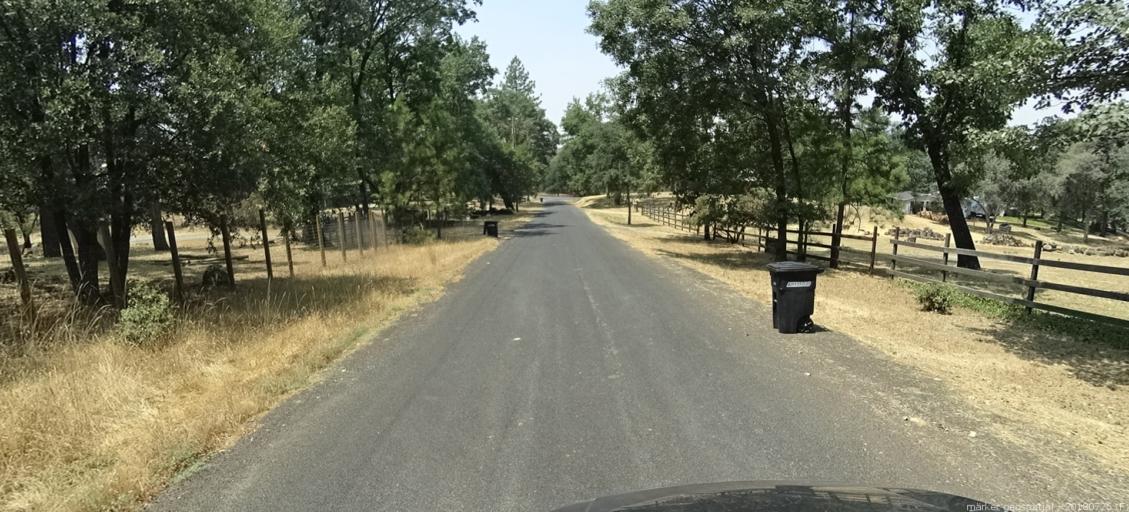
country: US
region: California
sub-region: Madera County
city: Oakhurst
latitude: 37.2845
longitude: -119.6296
